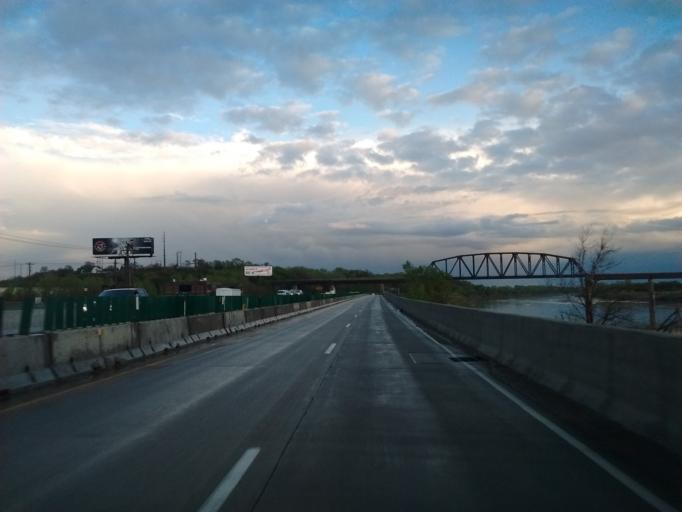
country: US
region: Iowa
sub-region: Woodbury County
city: Sioux City
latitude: 42.4790
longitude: -96.3872
